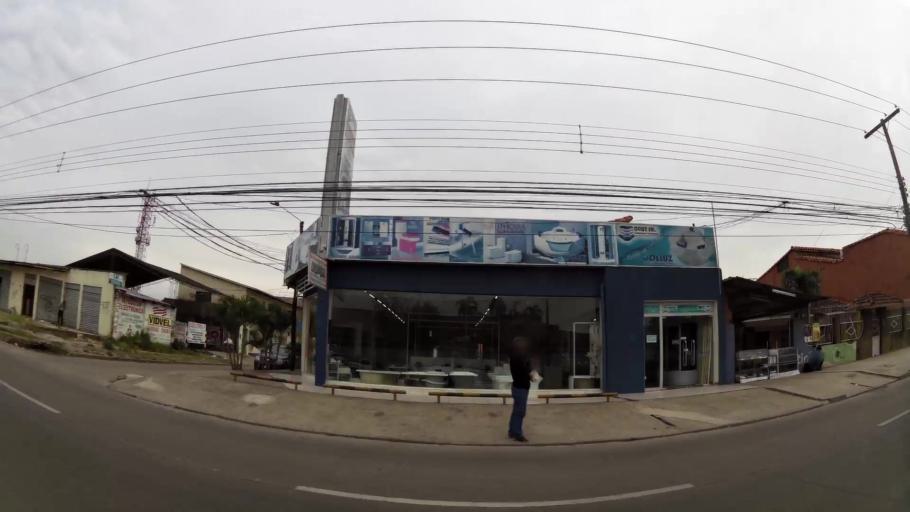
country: BO
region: Santa Cruz
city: Santa Cruz de la Sierra
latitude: -17.8052
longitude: -63.1802
